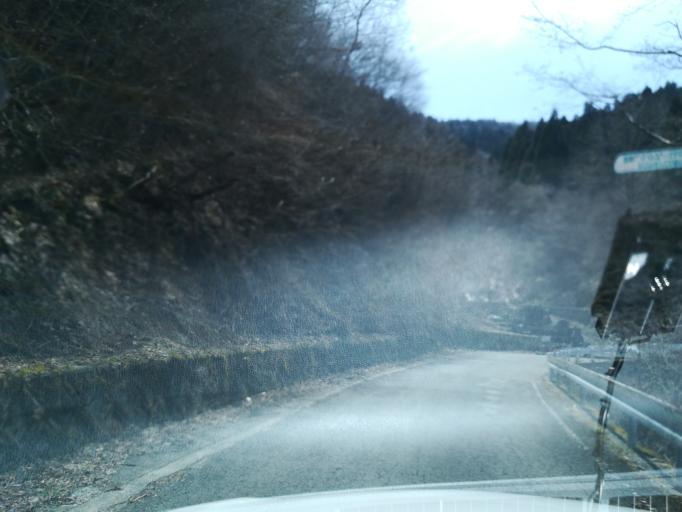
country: JP
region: Tokushima
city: Wakimachi
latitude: 33.8791
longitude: 134.0530
